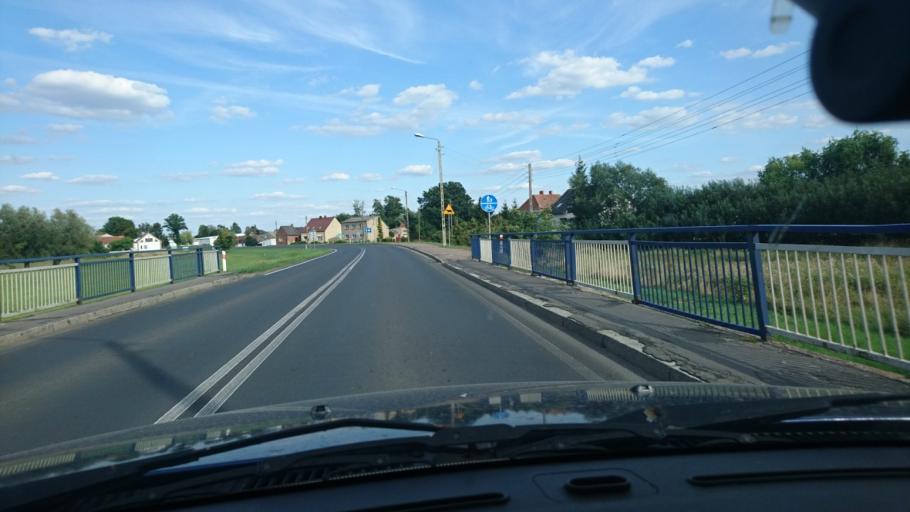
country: PL
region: Greater Poland Voivodeship
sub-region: Powiat krotoszynski
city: Kobylin
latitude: 51.7159
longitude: 17.2336
